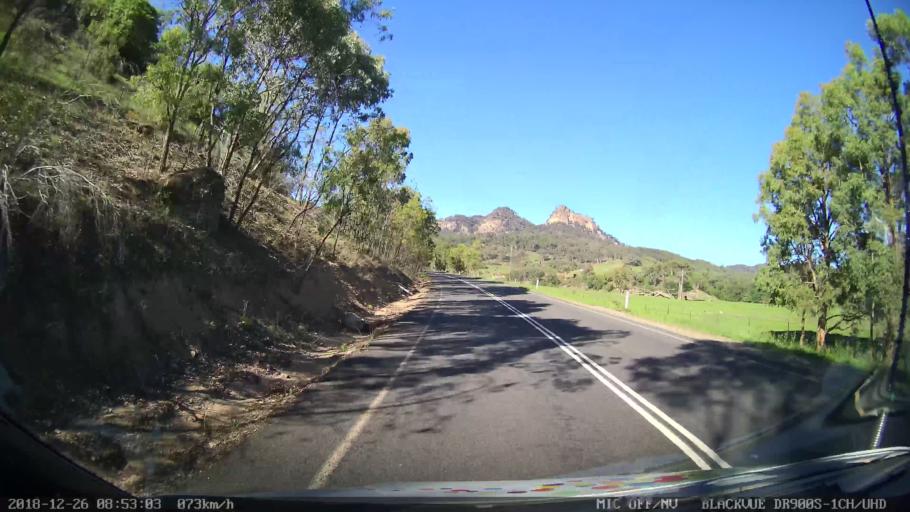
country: AU
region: New South Wales
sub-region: Mid-Western Regional
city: Kandos
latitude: -32.6004
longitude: 150.0801
